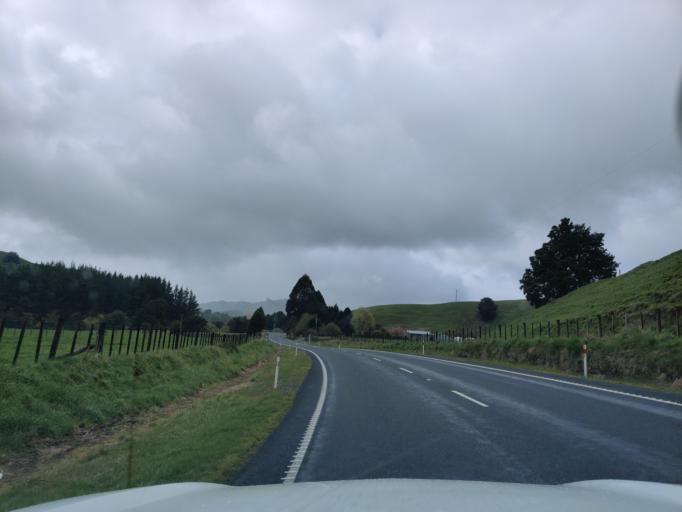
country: NZ
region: Waikato
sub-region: Otorohanga District
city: Otorohanga
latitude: -38.6934
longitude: 175.2157
